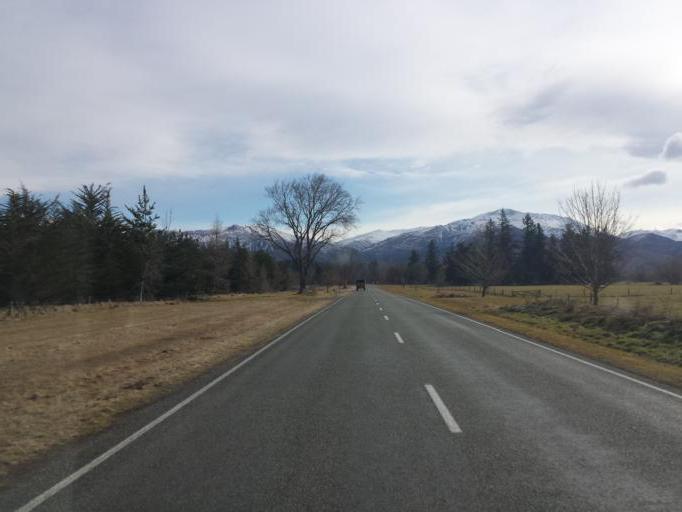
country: NZ
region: Canterbury
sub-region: Timaru District
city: Pleasant Point
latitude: -44.0509
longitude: 170.7645
